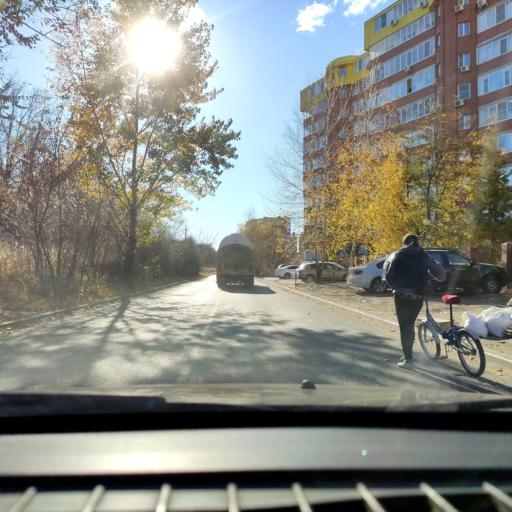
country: RU
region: Samara
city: Tol'yatti
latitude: 53.5185
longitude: 49.3162
